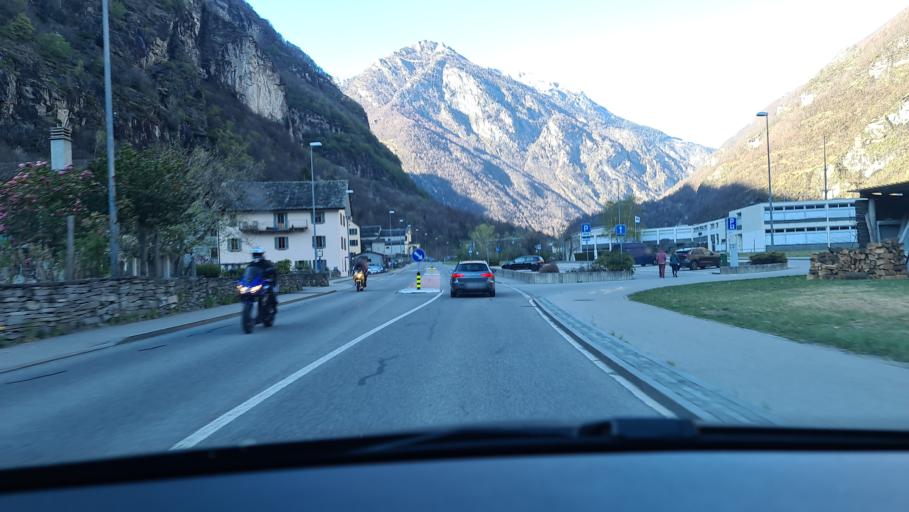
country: CH
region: Ticino
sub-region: Vallemaggia District
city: Cevio
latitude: 46.3195
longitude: 8.6023
